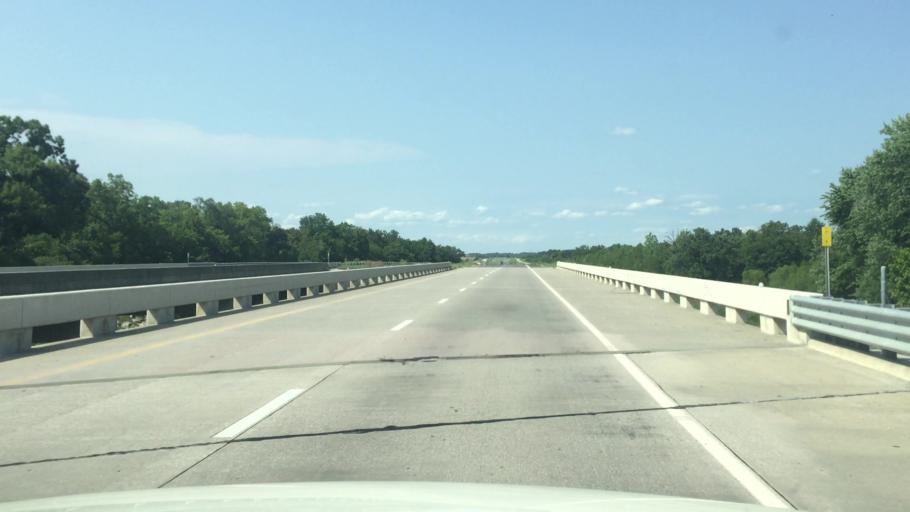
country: US
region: Kansas
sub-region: Linn County
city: La Cygne
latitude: 38.2993
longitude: -94.6773
